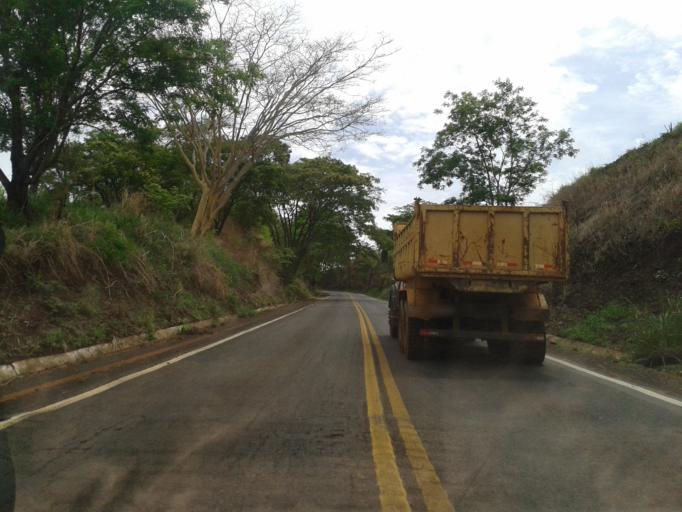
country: BR
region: Goias
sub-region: Buriti Alegre
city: Buriti Alegre
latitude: -18.1384
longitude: -48.9519
